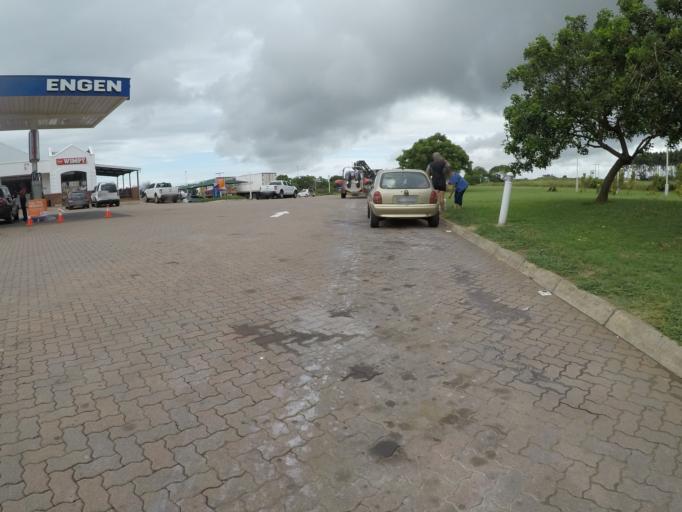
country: ZA
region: KwaZulu-Natal
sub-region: uThungulu District Municipality
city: Empangeni
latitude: -28.8144
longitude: 31.9145
